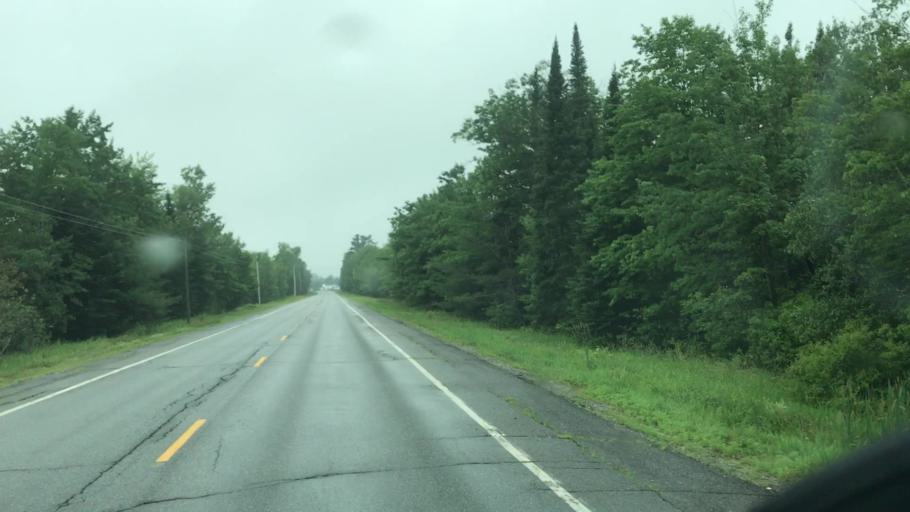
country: US
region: Maine
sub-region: Penobscot County
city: Enfield
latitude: 45.3045
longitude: -68.6135
